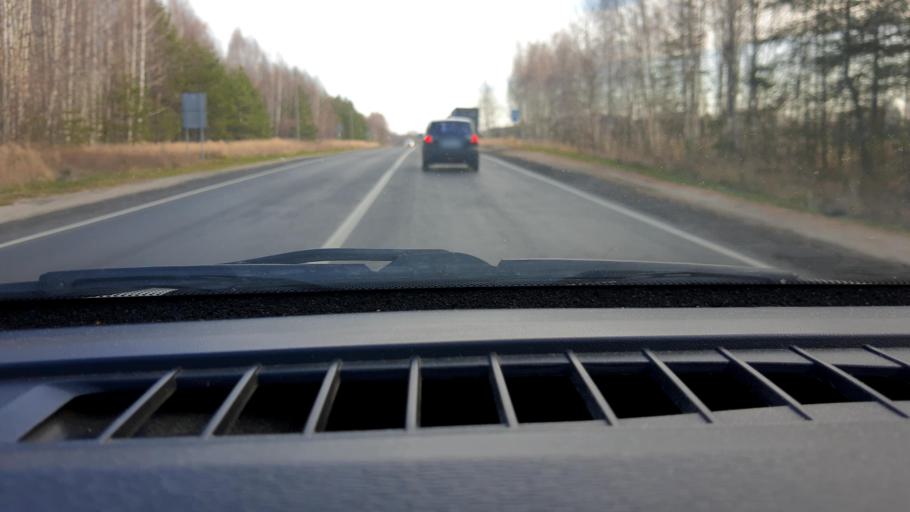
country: RU
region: Nizjnij Novgorod
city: Gorodets
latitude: 56.6137
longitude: 43.5891
